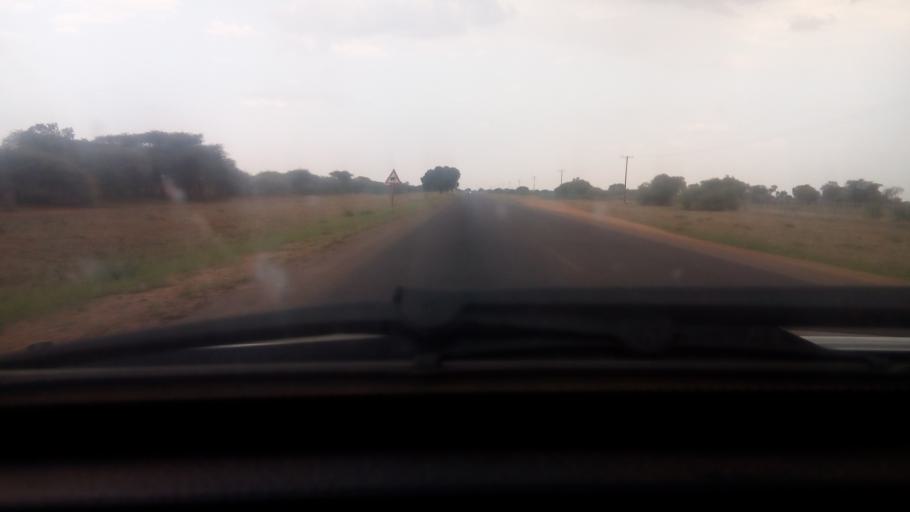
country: BW
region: Kweneng
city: Metsemotlhaba
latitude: -24.4735
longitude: 25.7057
